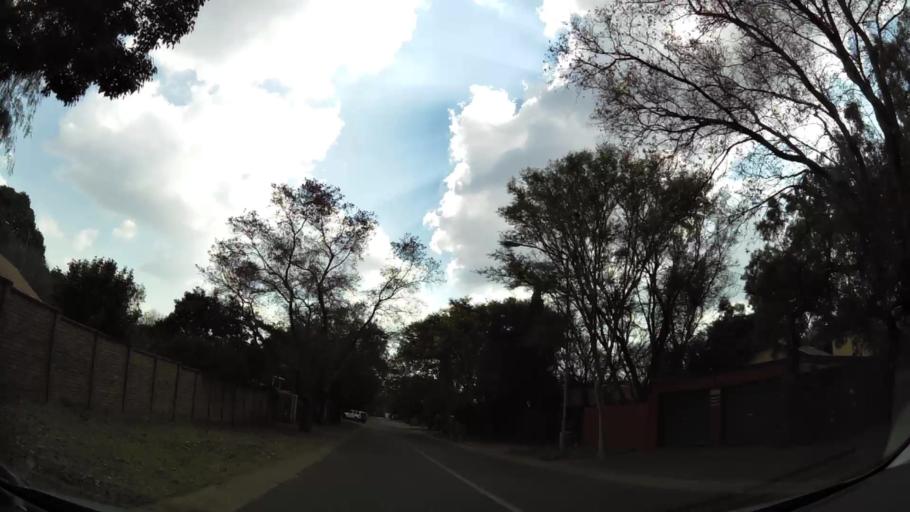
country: ZA
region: Gauteng
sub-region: City of Tshwane Metropolitan Municipality
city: Centurion
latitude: -25.8407
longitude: 28.2668
